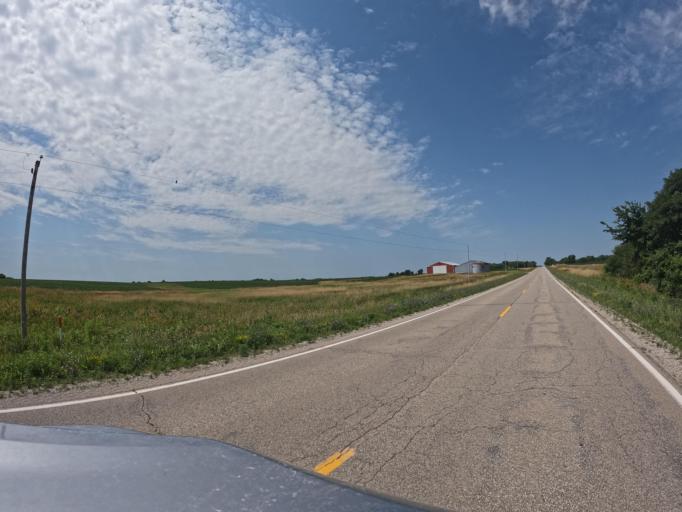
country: US
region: Iowa
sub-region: Appanoose County
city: Centerville
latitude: 40.8123
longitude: -92.9361
